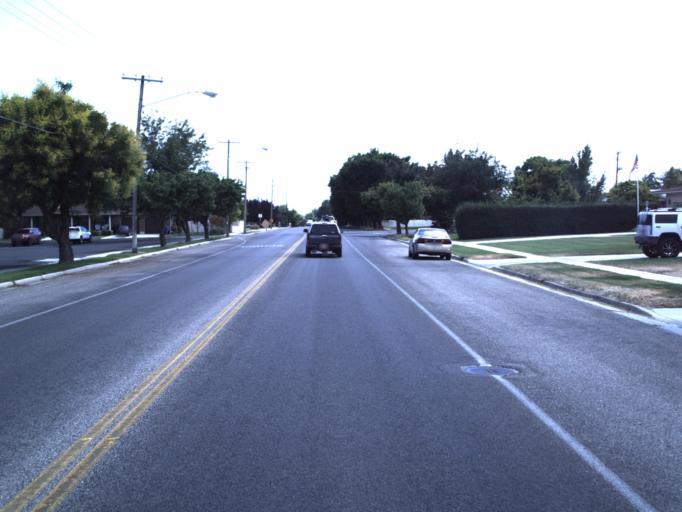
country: US
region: Utah
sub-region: Box Elder County
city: Tremonton
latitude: 41.7202
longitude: -112.1620
